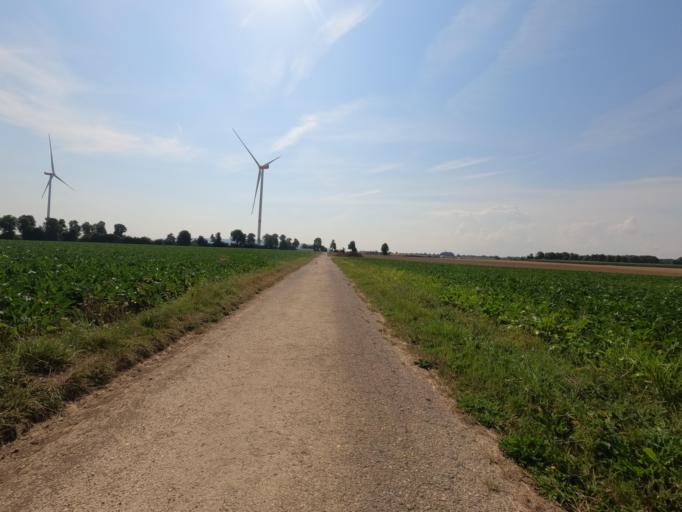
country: DE
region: North Rhine-Westphalia
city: Julich
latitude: 50.9763
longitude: 6.3705
